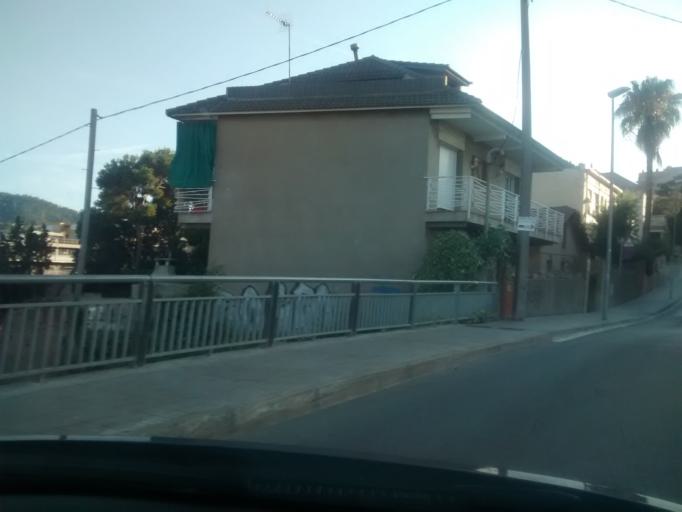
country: ES
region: Catalonia
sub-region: Provincia de Barcelona
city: Sant Vicenc dels Horts
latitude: 41.3920
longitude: 2.0091
